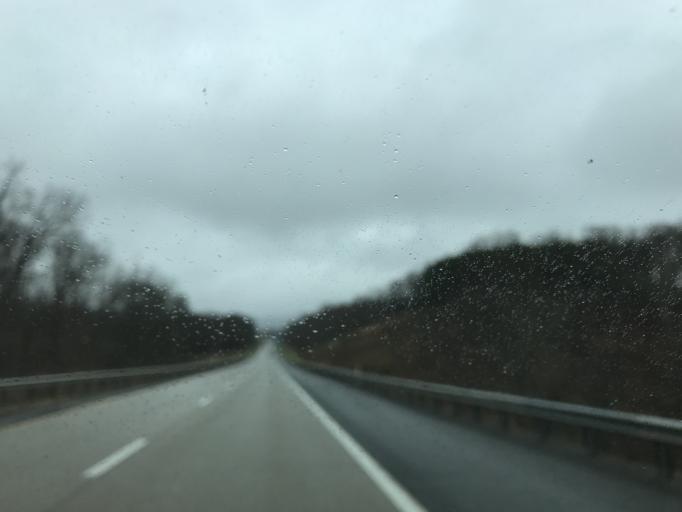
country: US
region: West Virginia
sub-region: Greenbrier County
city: Rainelle
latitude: 37.8908
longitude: -80.6610
